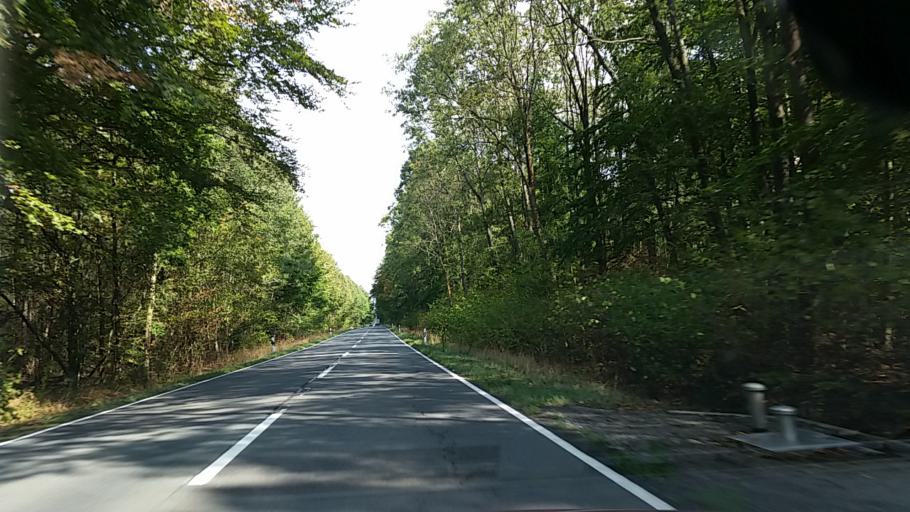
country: DE
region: Thuringia
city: Rossleben
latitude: 51.3403
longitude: 11.4882
